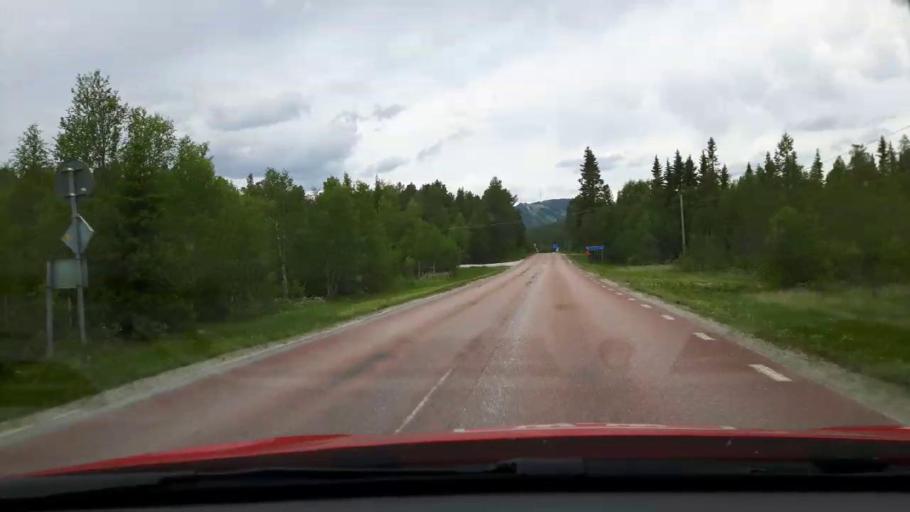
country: NO
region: Hedmark
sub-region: Engerdal
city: Engerdal
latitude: 62.5180
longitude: 12.5981
